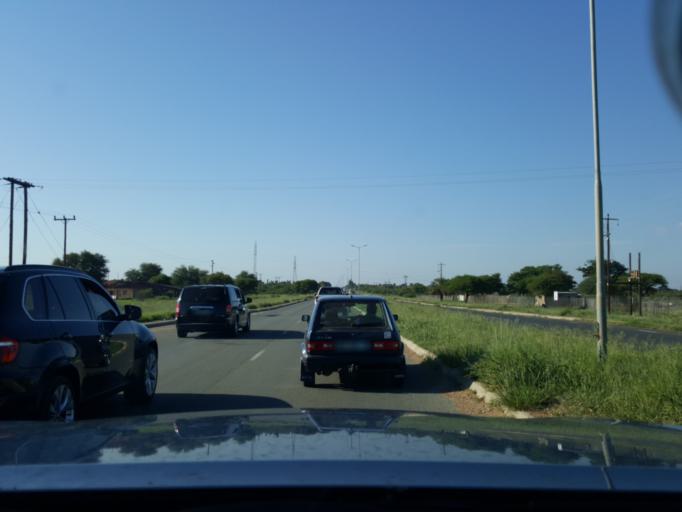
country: ZA
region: North-West
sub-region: Ngaka Modiri Molema District Municipality
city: Mmabatho
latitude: -25.8040
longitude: 25.6320
